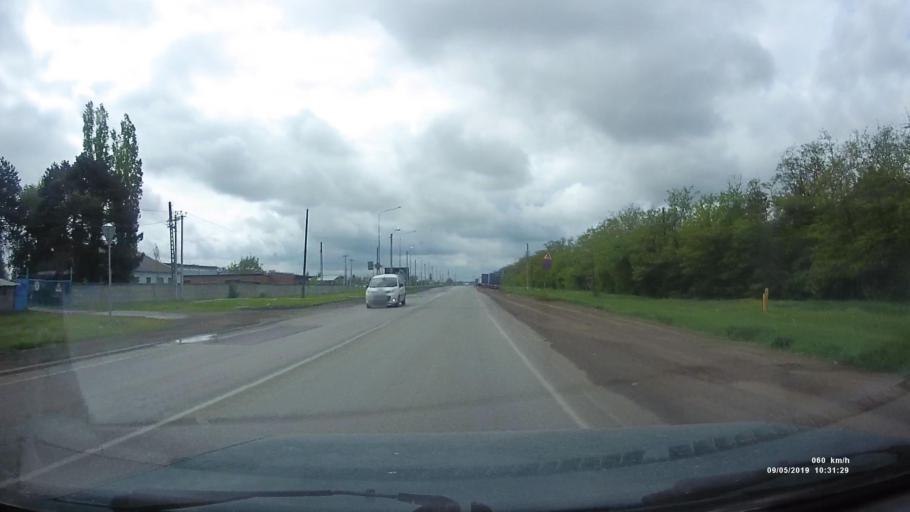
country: RU
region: Rostov
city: Azov
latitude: 47.0811
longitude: 39.4278
